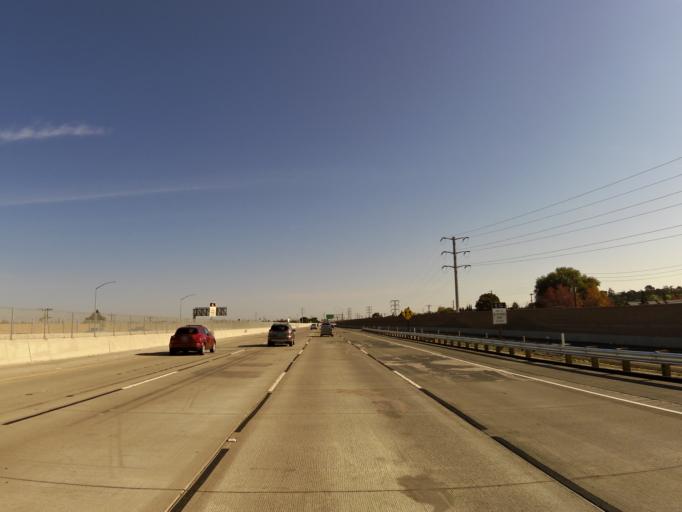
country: US
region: California
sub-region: Contra Costa County
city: Antioch
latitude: 37.9980
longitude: -121.8042
